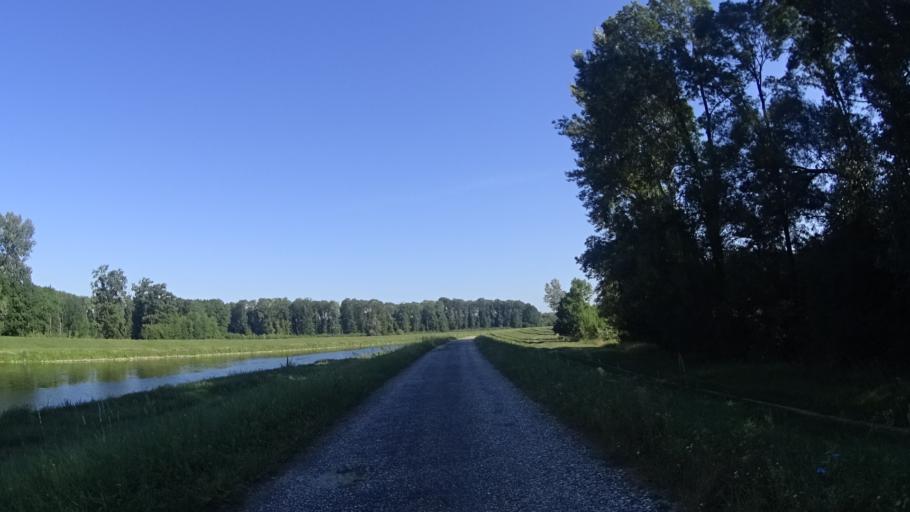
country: CZ
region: South Moravian
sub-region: Okres Breclav
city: Lanzhot
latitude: 48.7043
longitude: 16.9977
